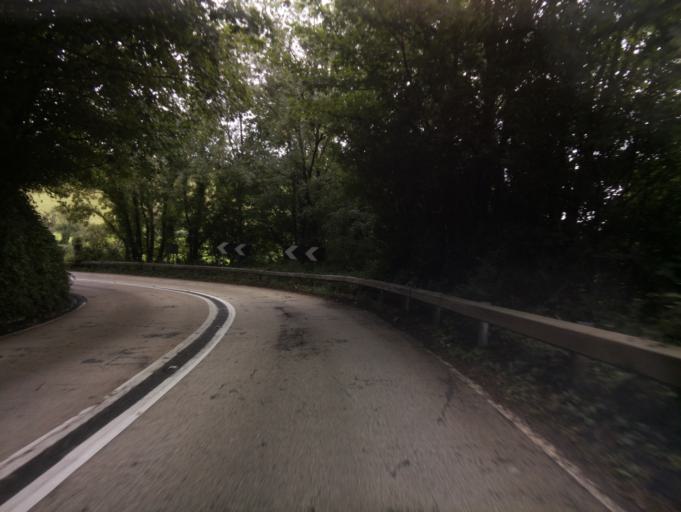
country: GB
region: England
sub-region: Devon
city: Modbury
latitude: 50.3464
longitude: -3.8890
